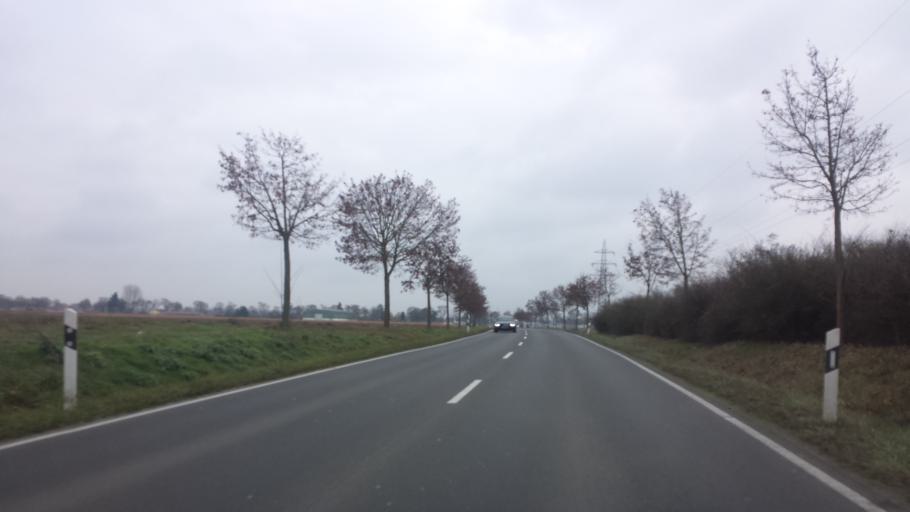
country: DE
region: Hesse
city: Lampertheim
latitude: 49.6026
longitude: 8.4850
